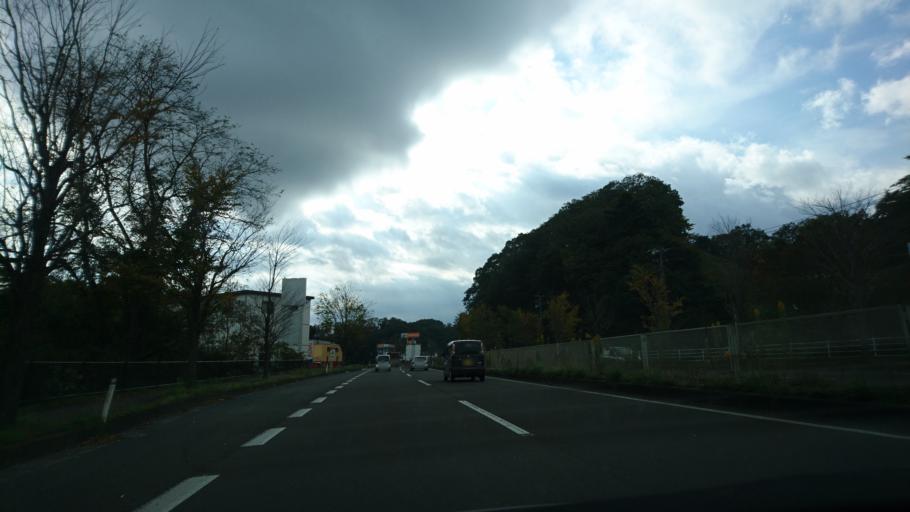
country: JP
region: Miyagi
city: Tomiya
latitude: 38.3769
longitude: 140.8733
